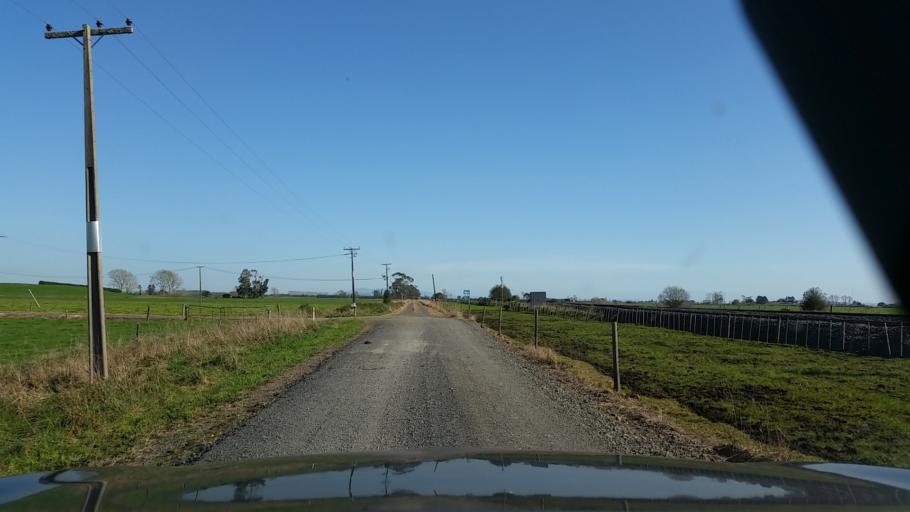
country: NZ
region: Waikato
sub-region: Waipa District
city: Cambridge
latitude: -37.6809
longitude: 175.4573
